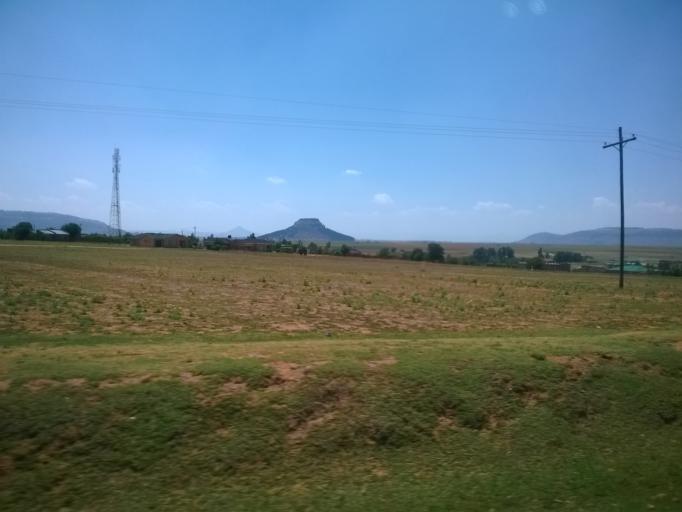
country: LS
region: Leribe
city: Maputsoe
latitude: -28.9704
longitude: 27.9694
